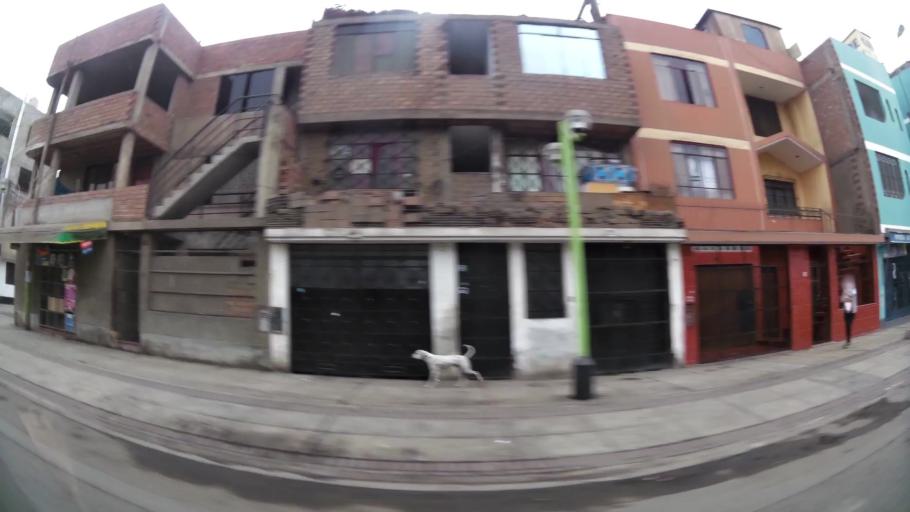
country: PE
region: Lima
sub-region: Lima
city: Vitarte
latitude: -12.0407
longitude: -76.9643
